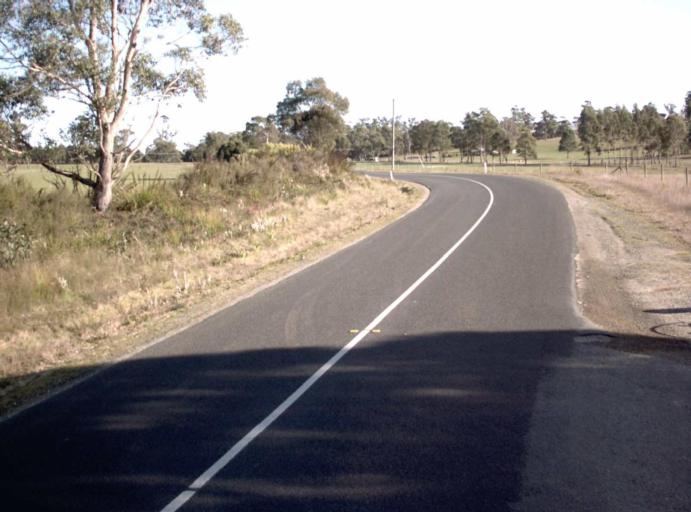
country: AU
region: Tasmania
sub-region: Dorset
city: Bridport
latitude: -41.1009
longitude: 147.1962
